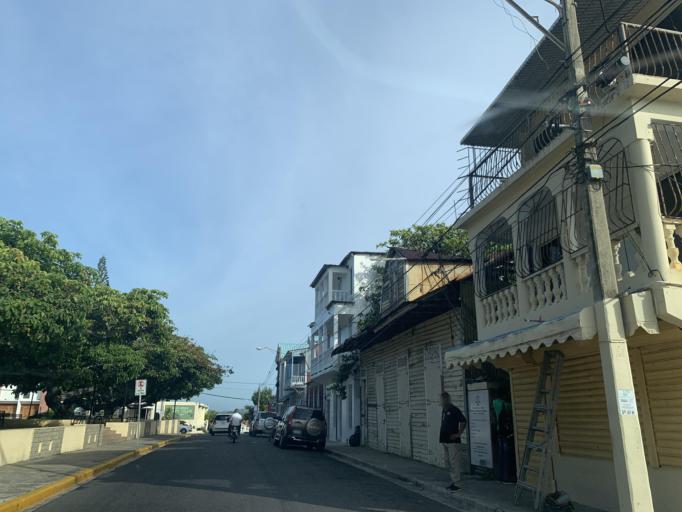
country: DO
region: Puerto Plata
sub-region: Puerto Plata
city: Puerto Plata
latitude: 19.7969
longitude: -70.6891
